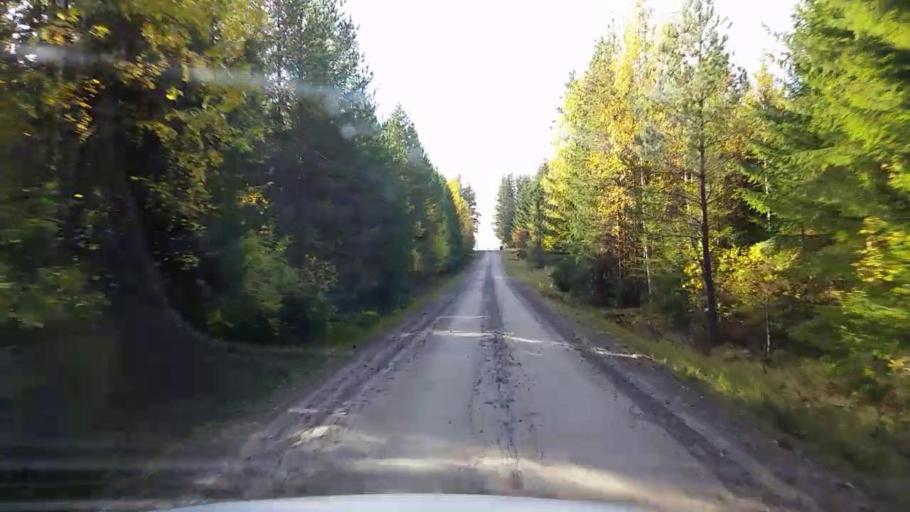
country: SE
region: Gaevleborg
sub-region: Ljusdals Kommun
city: Jaervsoe
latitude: 61.7868
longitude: 16.1680
